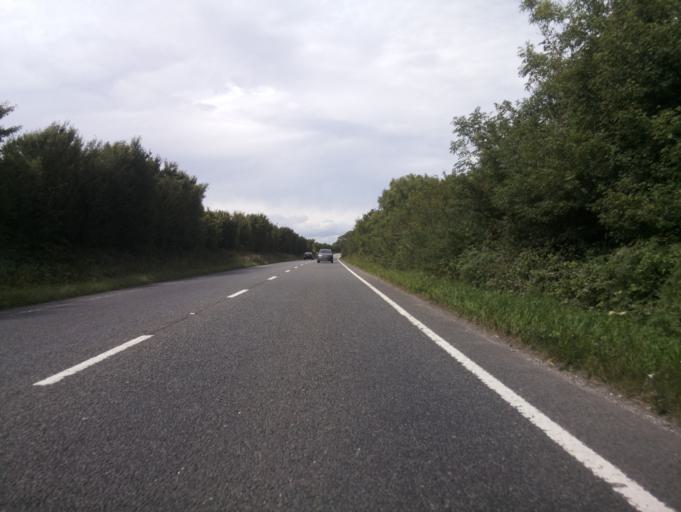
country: GB
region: England
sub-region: Dorset
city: Sherborne
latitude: 50.8123
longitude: -2.5546
